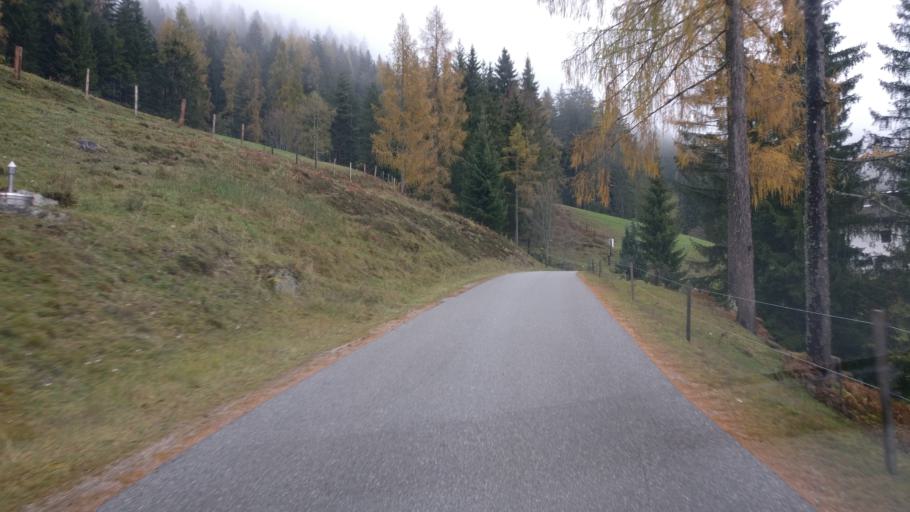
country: AT
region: Salzburg
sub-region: Politischer Bezirk Sankt Johann im Pongau
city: Filzmoos
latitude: 47.4000
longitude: 13.5201
